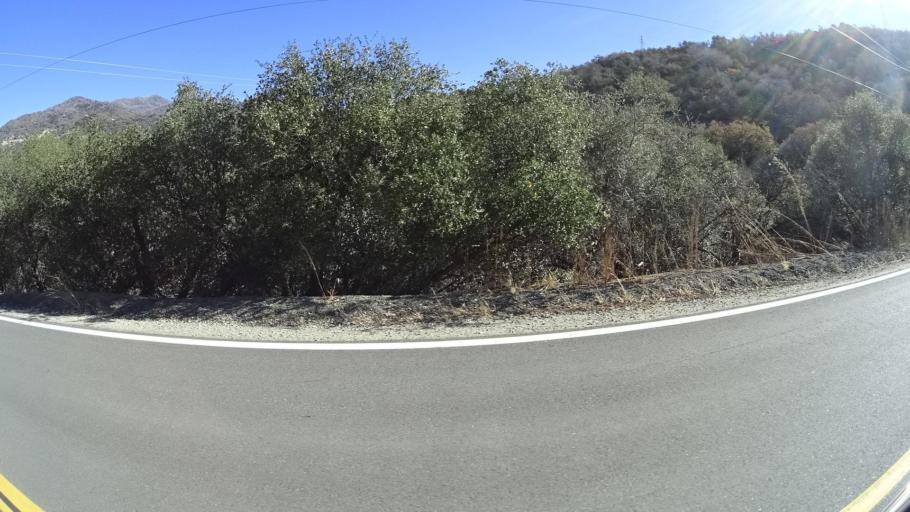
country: US
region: California
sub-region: Kern County
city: Alta Sierra
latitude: 35.7367
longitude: -118.6466
